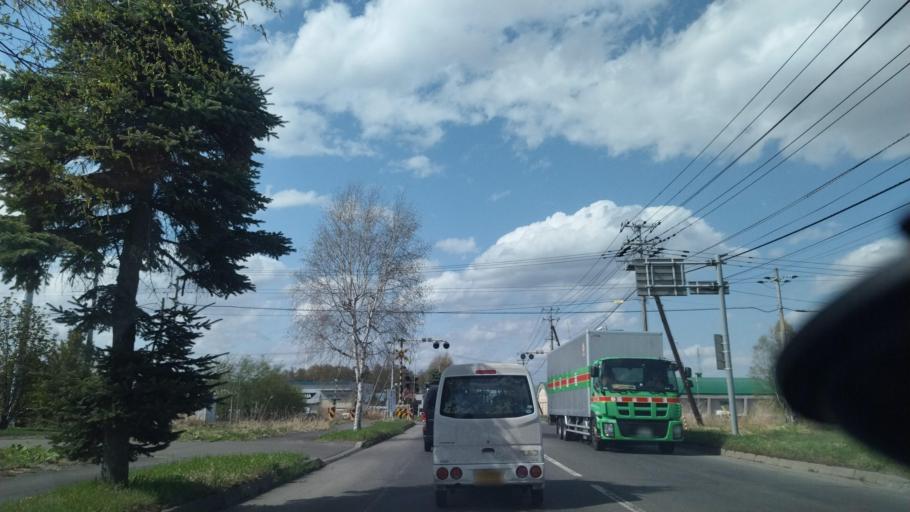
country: JP
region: Hokkaido
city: Obihiro
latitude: 42.9246
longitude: 143.1436
